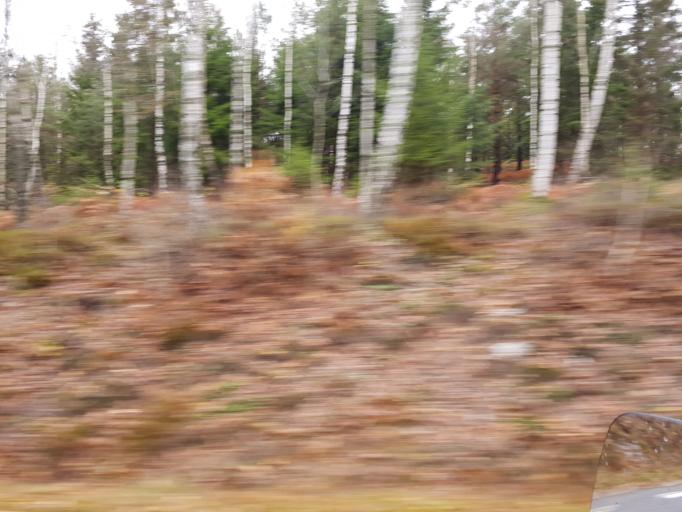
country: SE
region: Vaestra Goetaland
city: Svanesund
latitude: 58.2063
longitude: 11.8131
